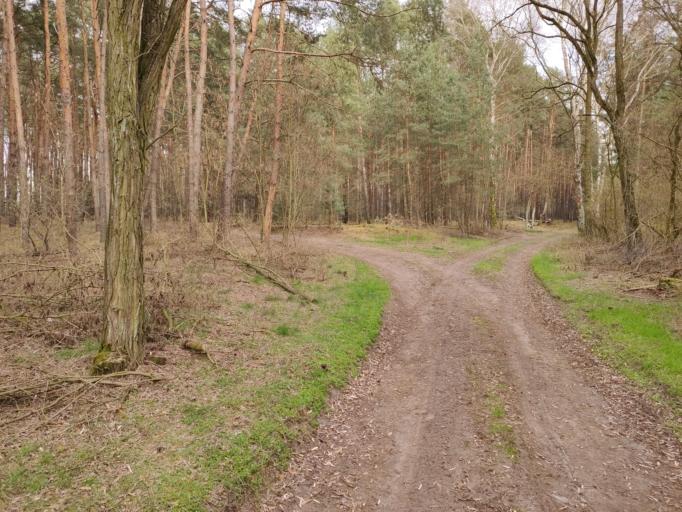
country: PL
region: Greater Poland Voivodeship
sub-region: Powiat sredzki
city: Sroda Wielkopolska
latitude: 52.1451
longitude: 17.2695
